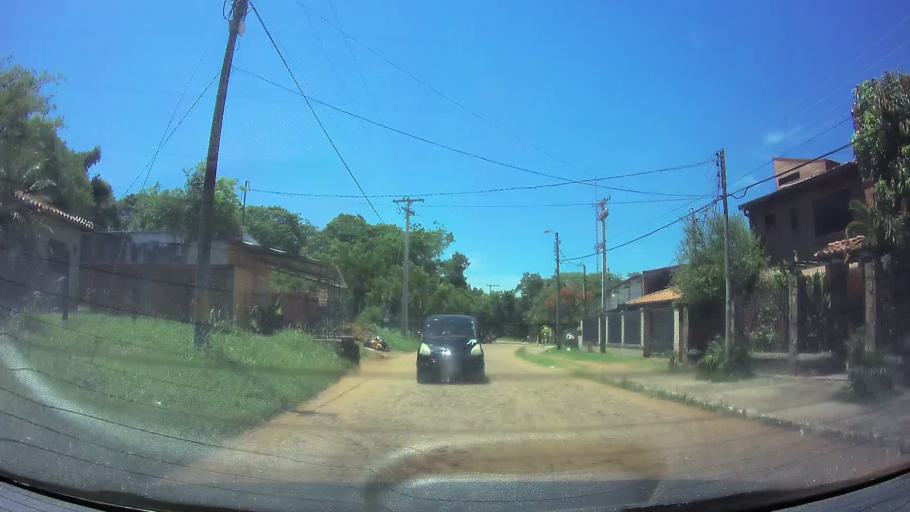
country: PY
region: Central
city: Limpio
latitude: -25.2454
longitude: -57.4862
